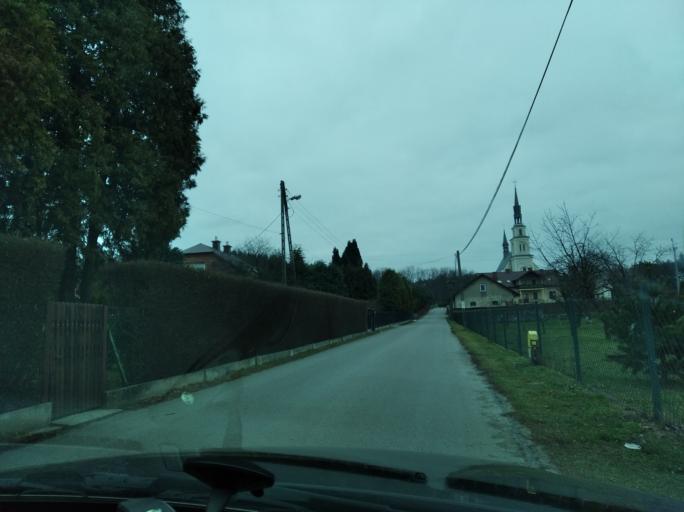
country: PL
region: Subcarpathian Voivodeship
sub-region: Powiat lancucki
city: Rakszawa
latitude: 50.1541
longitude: 22.2422
